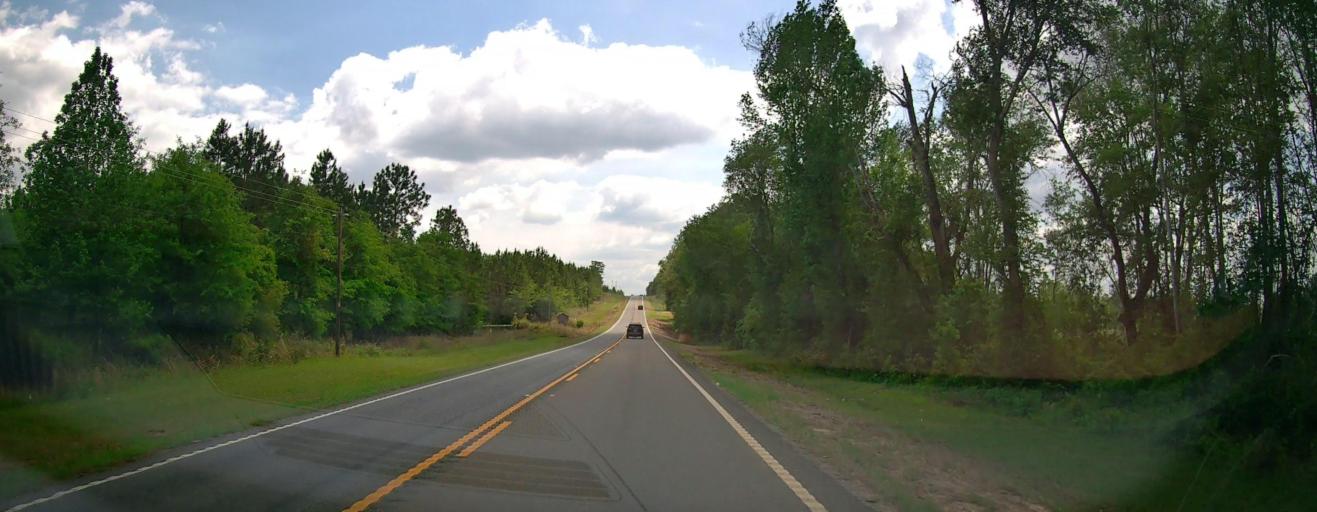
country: US
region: Georgia
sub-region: Treutlen County
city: Soperton
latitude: 32.4275
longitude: -82.6081
